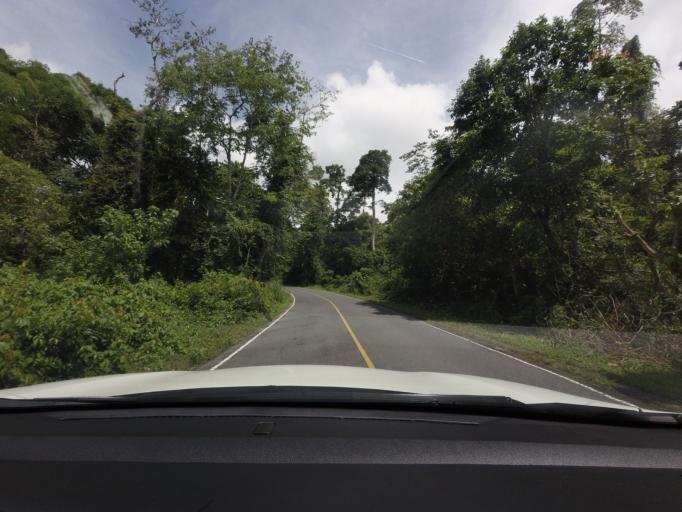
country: TH
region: Nakhon Nayok
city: Pak Phli
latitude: 14.3196
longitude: 101.3735
